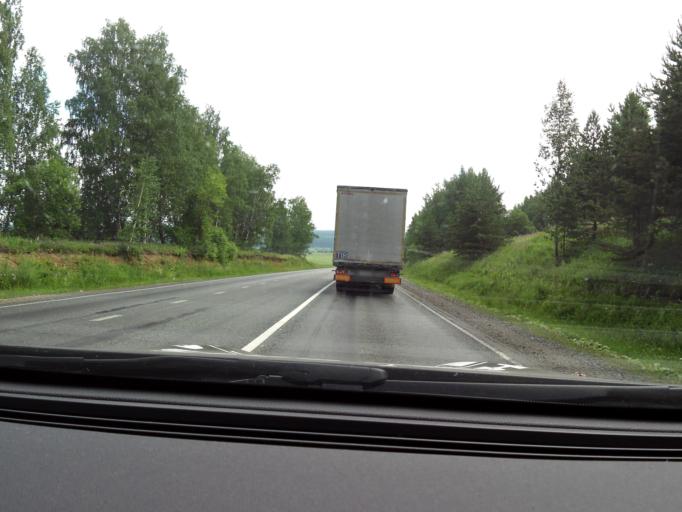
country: RU
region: Perm
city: Suksun
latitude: 57.0833
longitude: 57.4035
